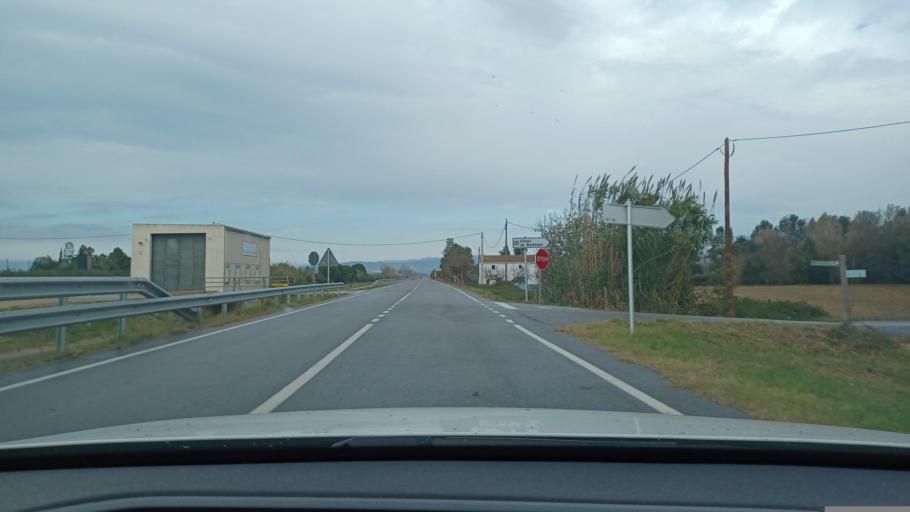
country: ES
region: Catalonia
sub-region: Provincia de Tarragona
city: Amposta
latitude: 40.6709
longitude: 0.5907
